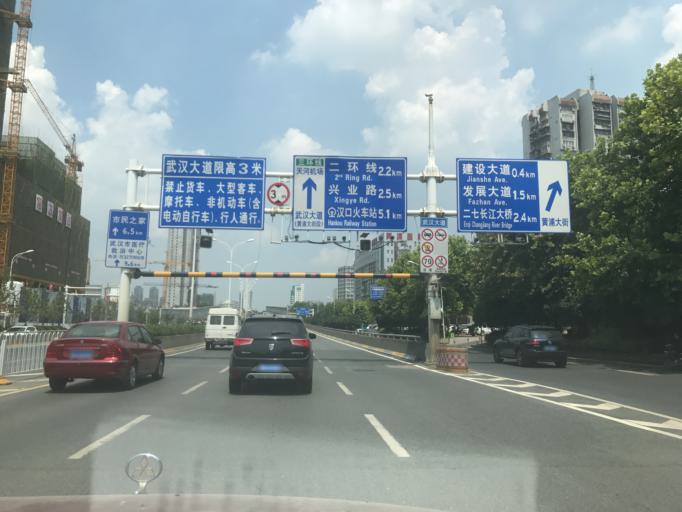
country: CN
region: Hubei
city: Jiang'an
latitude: 30.6196
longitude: 114.2964
